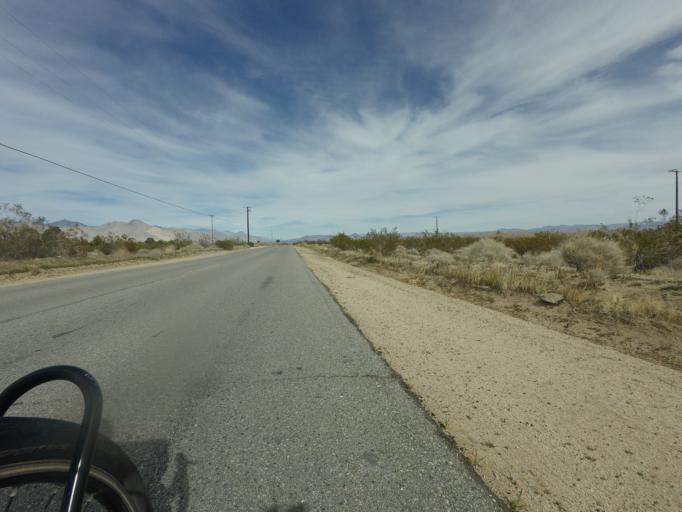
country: US
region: California
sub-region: Kern County
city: Inyokern
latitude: 35.7006
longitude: -117.8282
